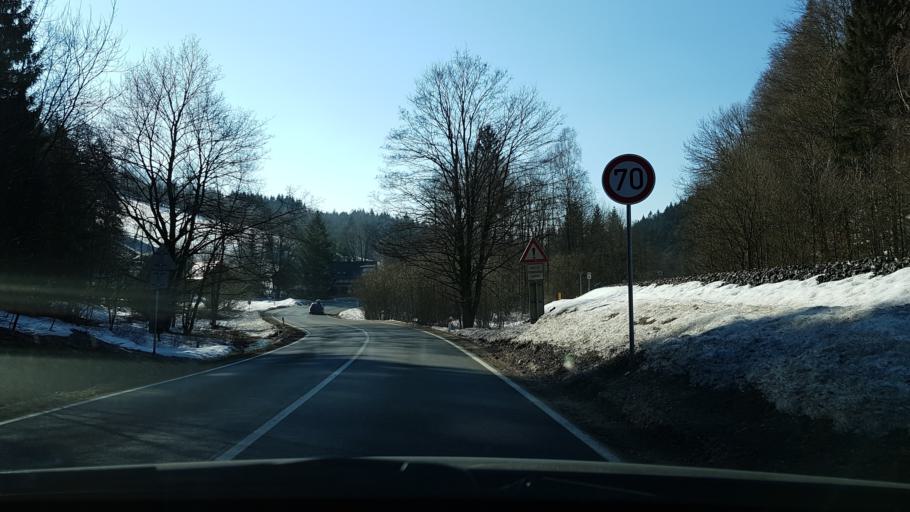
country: CZ
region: Olomoucky
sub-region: Okres Sumperk
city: Stare Mesto
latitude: 50.1354
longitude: 17.0128
